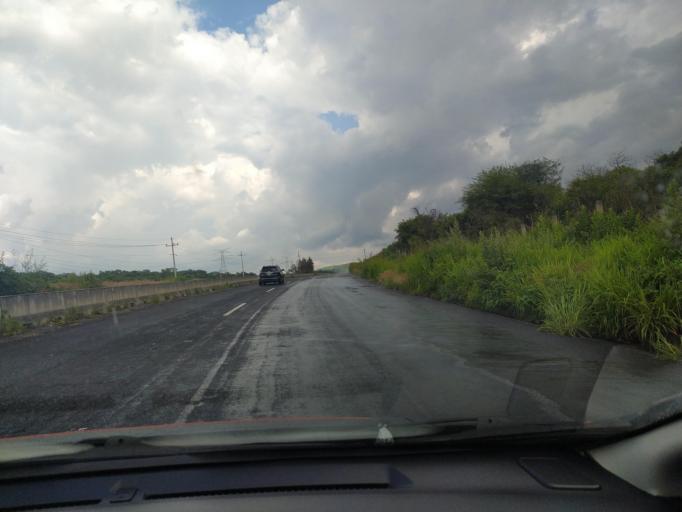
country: MX
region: Jalisco
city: Bellavista
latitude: 20.4337
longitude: -103.5967
